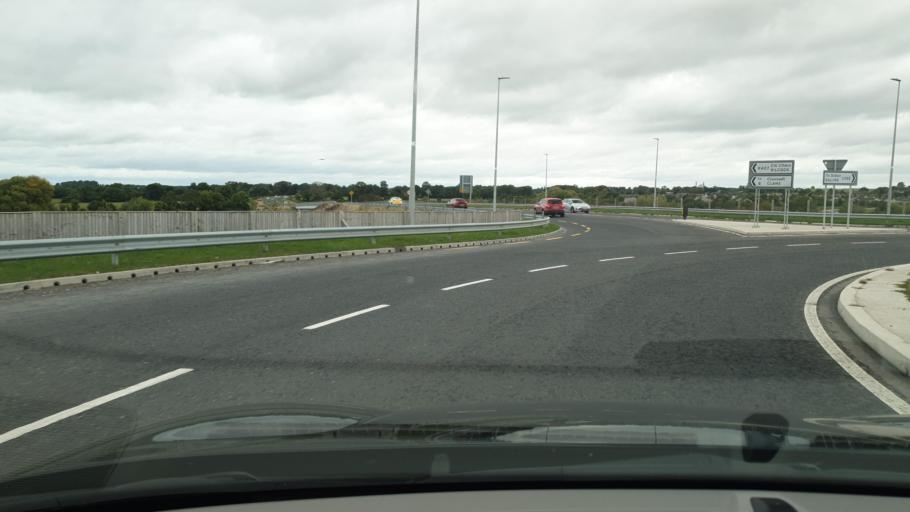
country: IE
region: Leinster
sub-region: Kildare
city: Sallins
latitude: 53.2481
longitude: -6.6813
